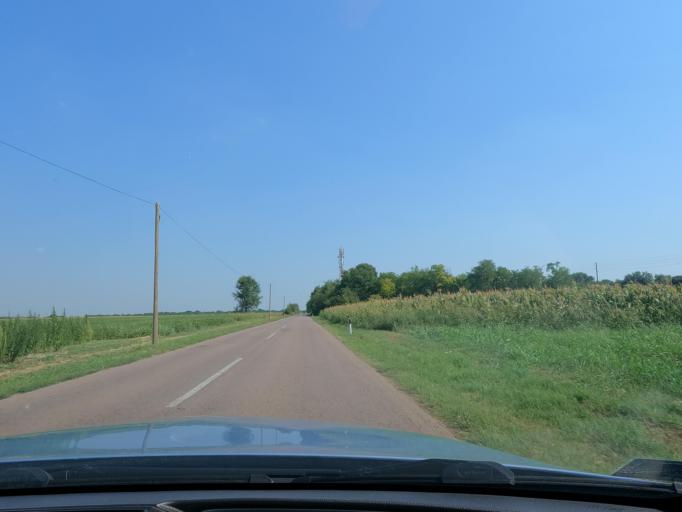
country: RS
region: Autonomna Pokrajina Vojvodina
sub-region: Severnobacki Okrug
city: Mali Igos
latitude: 45.7705
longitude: 19.7348
